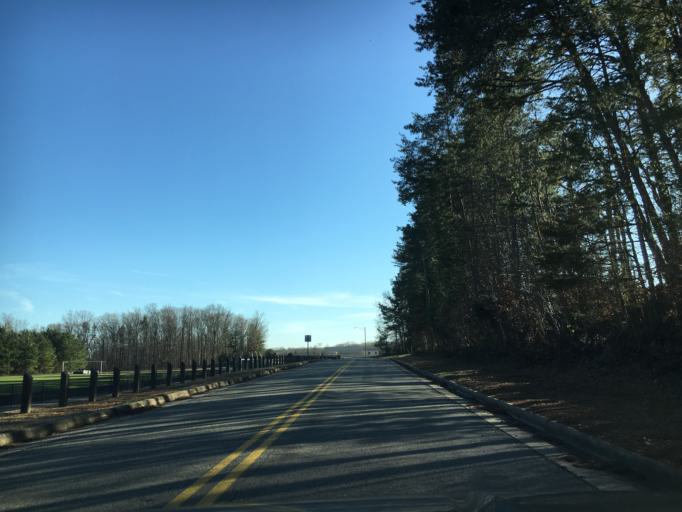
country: US
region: Virginia
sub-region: Halifax County
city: South Boston
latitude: 36.7299
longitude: -78.9142
